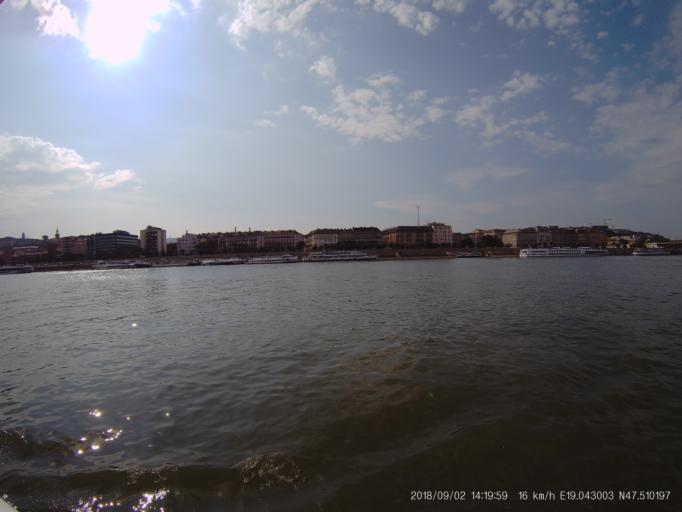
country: HU
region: Budapest
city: Budapest II. keruelet
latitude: 47.5099
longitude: 19.0434
